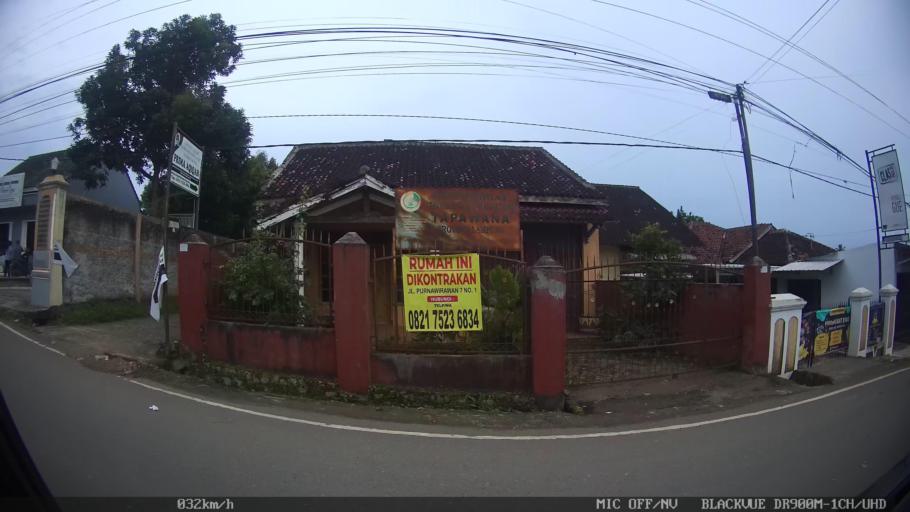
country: ID
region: Lampung
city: Kedaton
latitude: -5.3795
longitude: 105.2354
